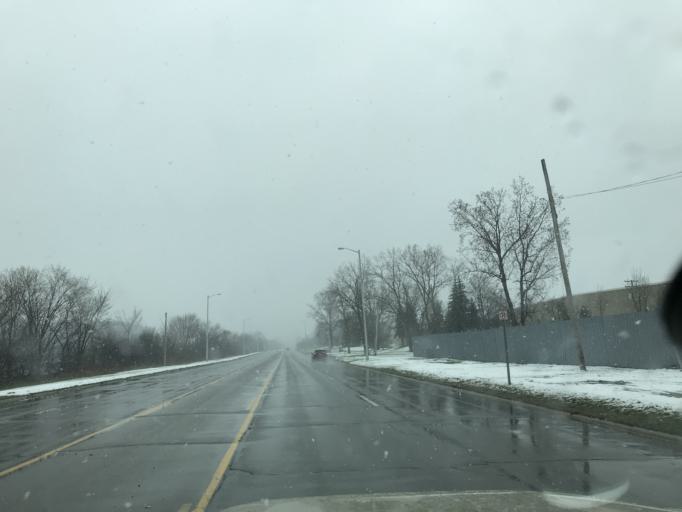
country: US
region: Michigan
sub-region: Wayne County
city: Woodhaven
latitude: 42.1806
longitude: -83.2276
